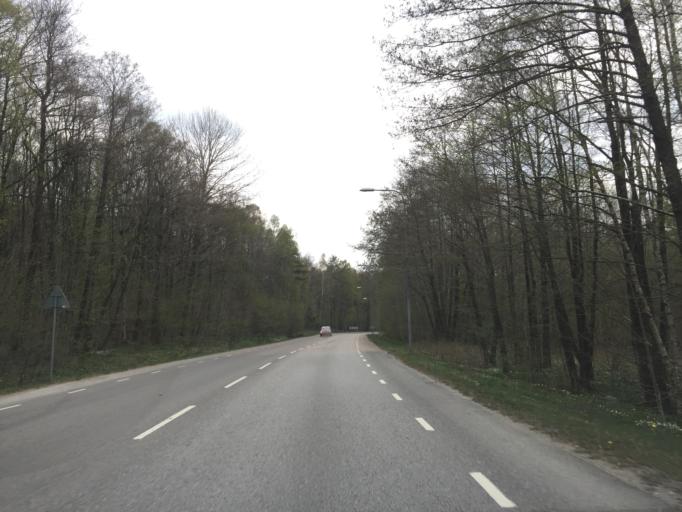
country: SE
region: Vaestra Goetaland
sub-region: Goteborg
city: Loevgaerdet
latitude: 57.8087
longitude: 12.0398
